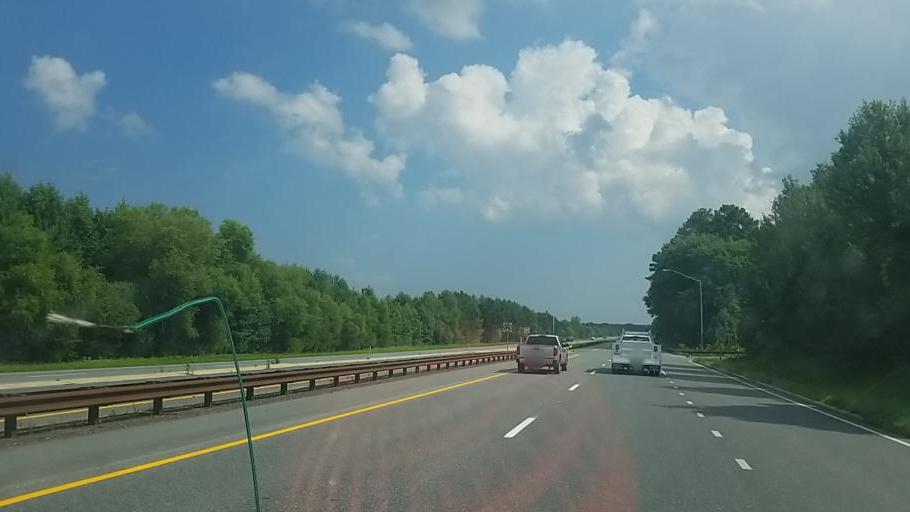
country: US
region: Delaware
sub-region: Sussex County
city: Selbyville
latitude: 38.4227
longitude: -75.2164
